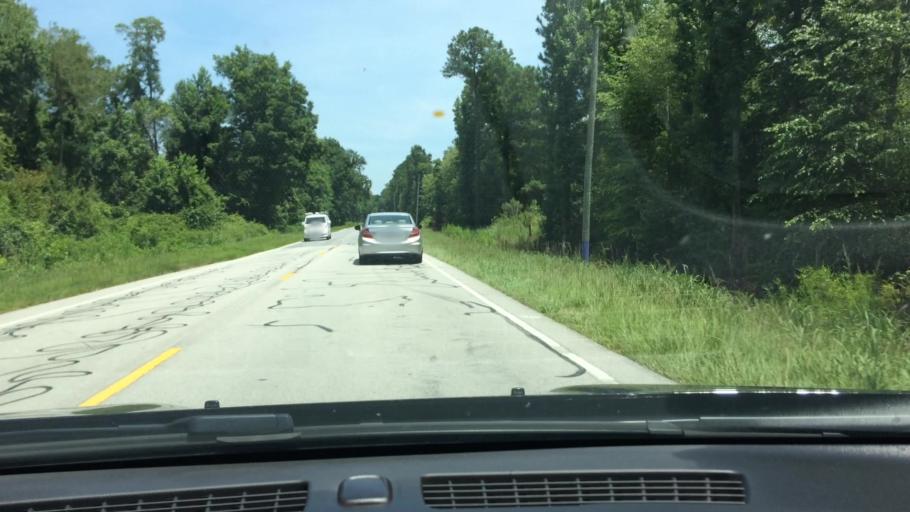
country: US
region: North Carolina
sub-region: Beaufort County
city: Washington
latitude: 35.5807
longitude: -77.1707
